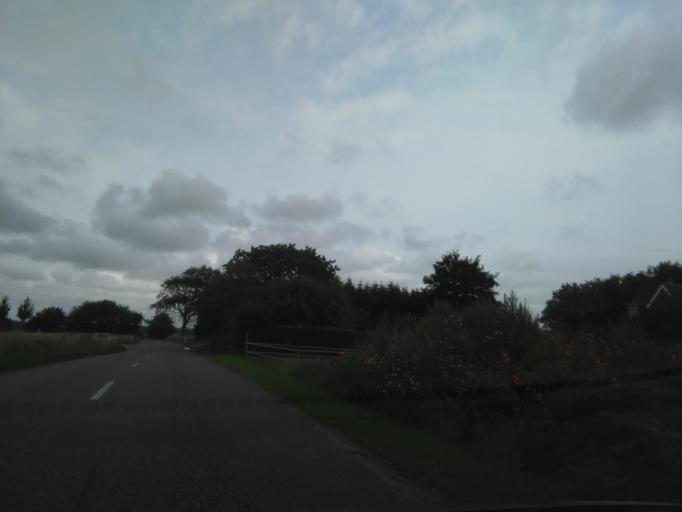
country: DK
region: Central Jutland
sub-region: Odder Kommune
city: Odder
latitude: 55.9529
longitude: 10.1102
